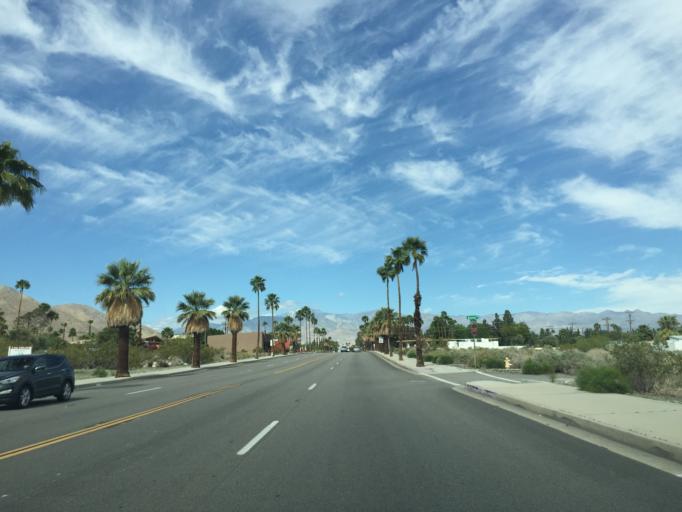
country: US
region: California
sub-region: Riverside County
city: Palm Springs
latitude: 33.8543
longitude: -116.5536
